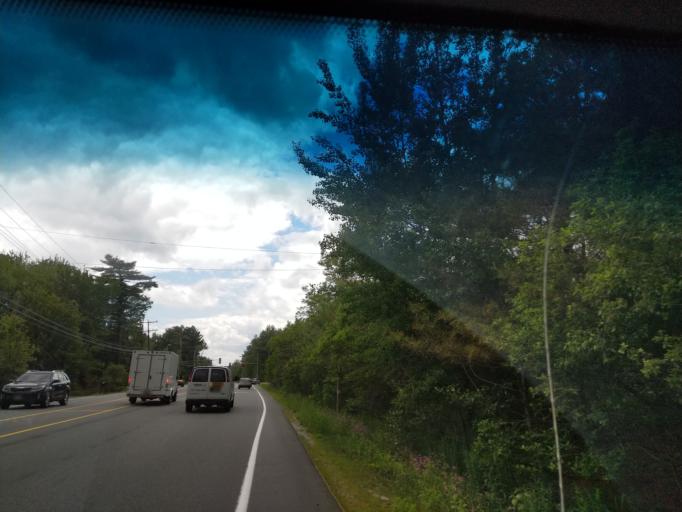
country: US
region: Maine
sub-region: Cumberland County
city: South Portland Gardens
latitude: 43.6214
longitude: -70.3372
